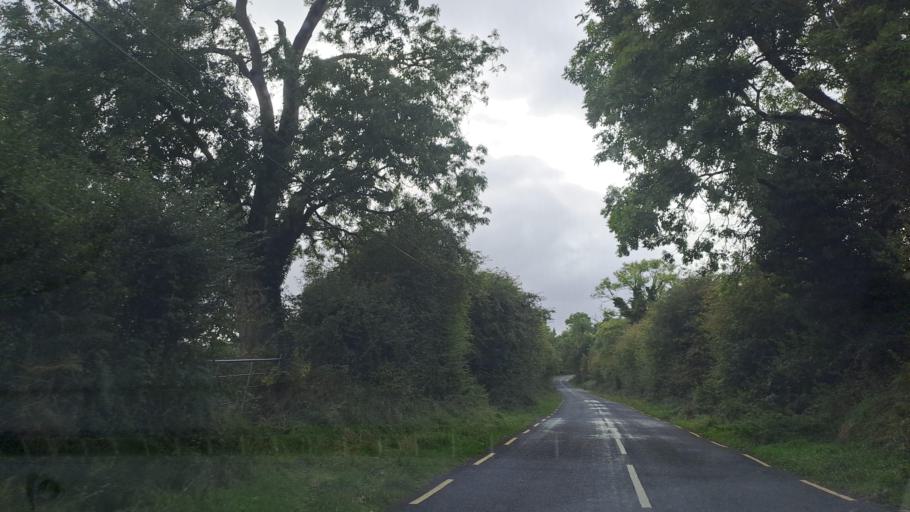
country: IE
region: Ulster
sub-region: County Monaghan
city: Carrickmacross
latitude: 54.0155
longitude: -6.7173
